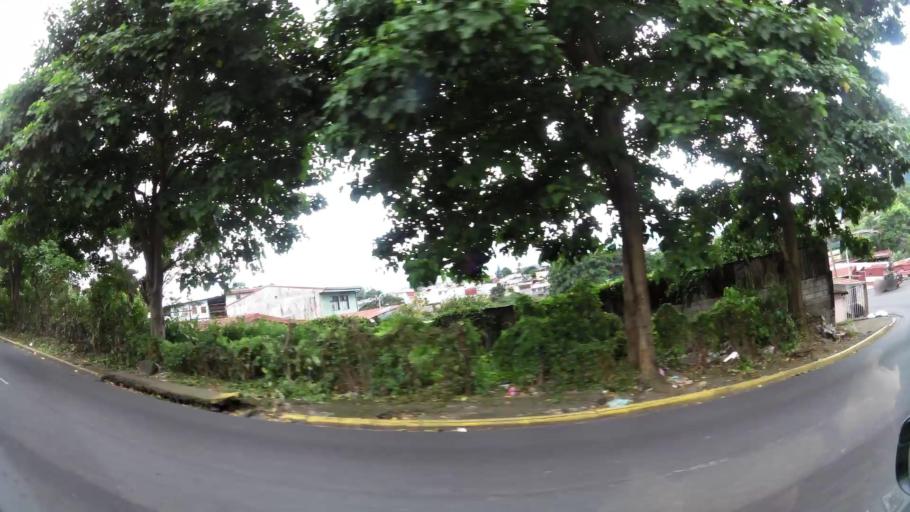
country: CR
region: San Jose
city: Alajuelita
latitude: 9.9024
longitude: -84.0902
